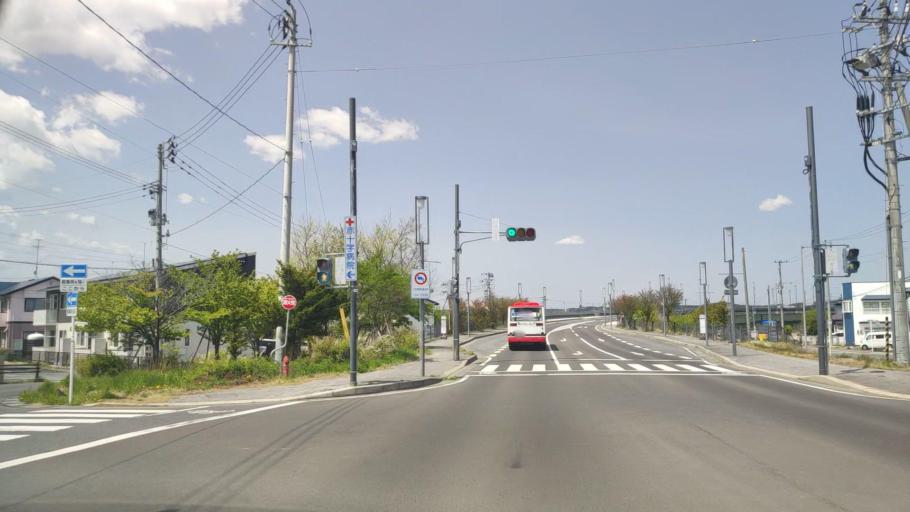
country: JP
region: Aomori
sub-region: Hachinohe Shi
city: Uchimaru
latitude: 40.4992
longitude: 141.4455
